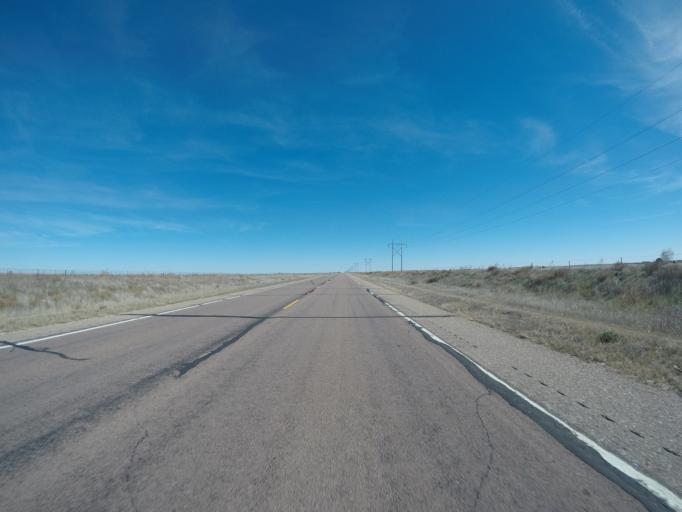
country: US
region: Colorado
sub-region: Yuma County
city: Yuma
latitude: 39.6549
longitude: -102.7963
